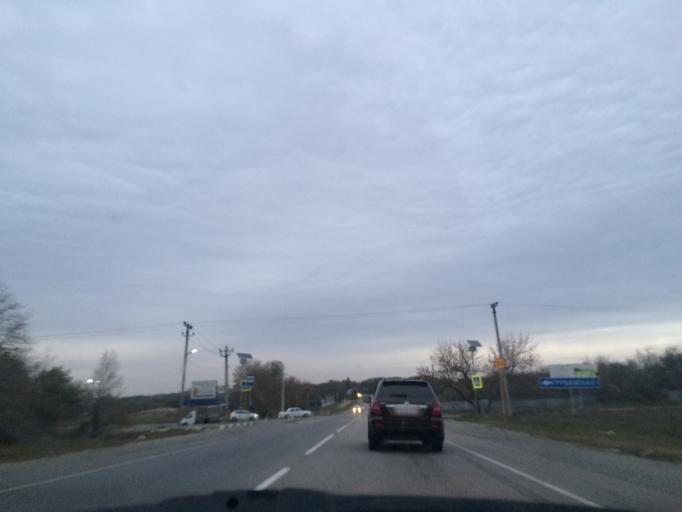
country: RU
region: Rostov
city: Grushevskaya
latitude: 47.4193
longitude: 40.0132
